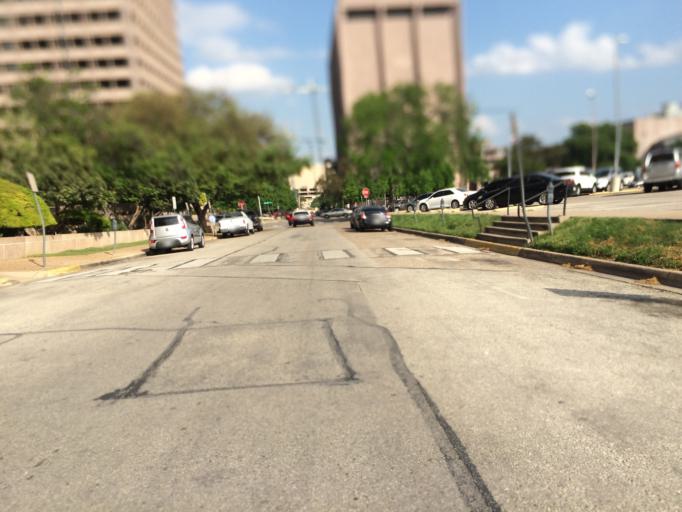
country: US
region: Texas
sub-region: Travis County
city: Austin
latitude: 30.2790
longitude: -97.7397
